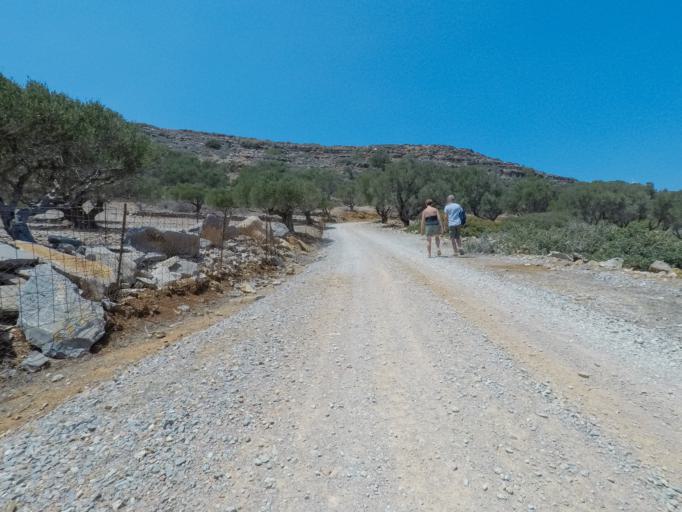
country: GR
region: Crete
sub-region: Nomos Lasithiou
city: Elounda
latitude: 35.3255
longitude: 25.7610
